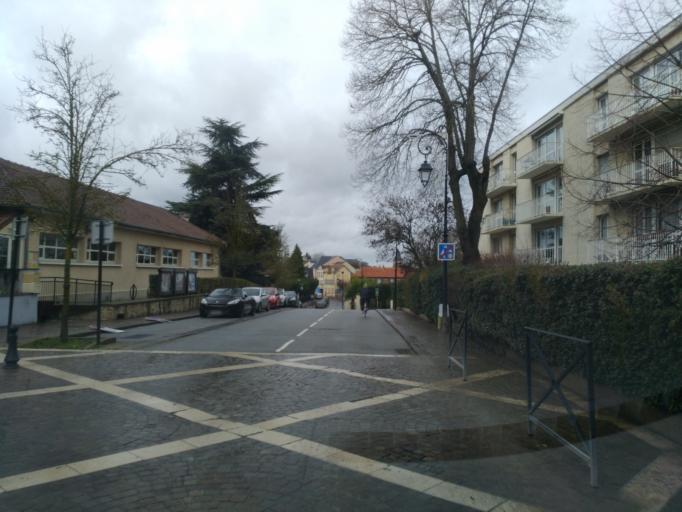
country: FR
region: Ile-de-France
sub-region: Departement des Yvelines
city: Chambourcy
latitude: 48.9040
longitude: 2.0431
